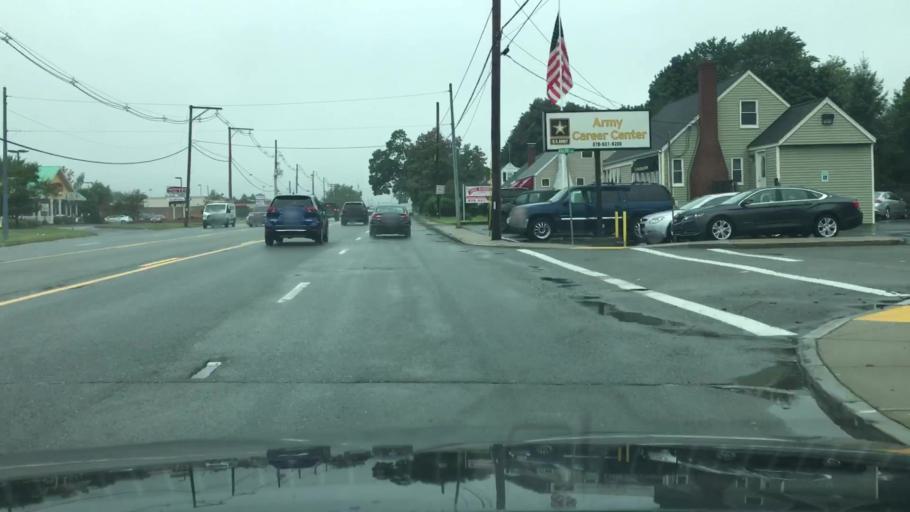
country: US
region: Massachusetts
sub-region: Essex County
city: Peabody
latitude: 42.5493
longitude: -70.9529
